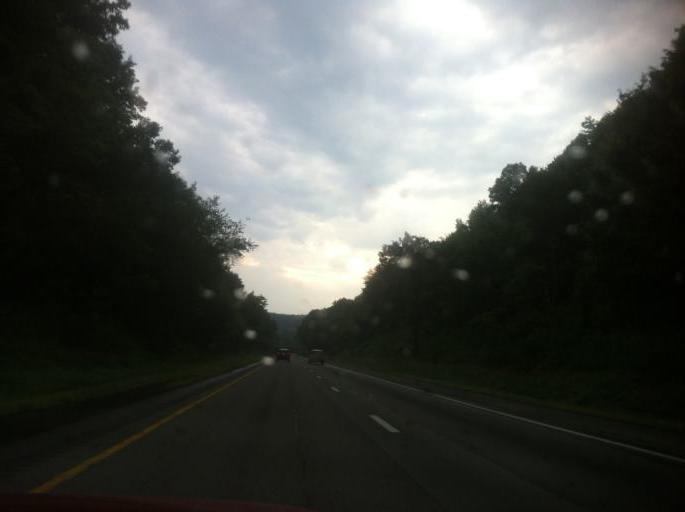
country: US
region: Pennsylvania
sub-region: Jefferson County
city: Brookville
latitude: 41.1439
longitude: -78.9822
